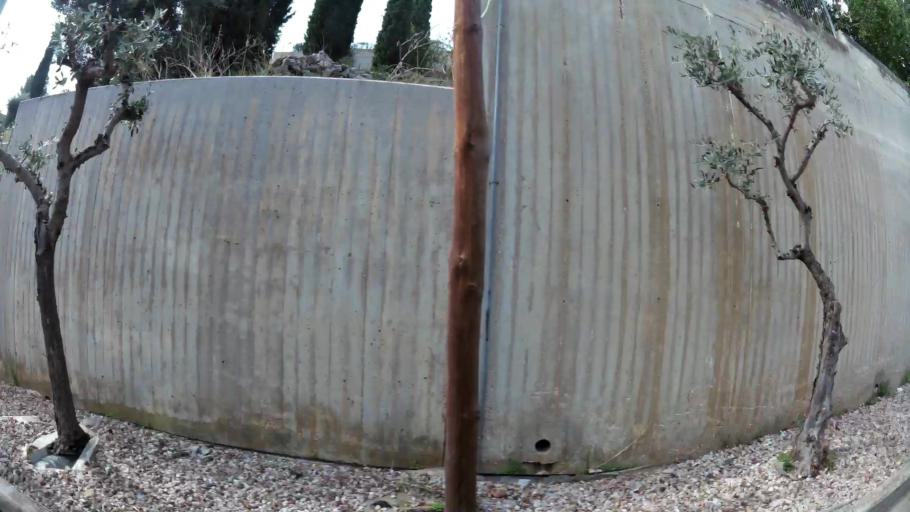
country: GR
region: Attica
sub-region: Nomarchia Athinas
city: Psychiko
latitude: 38.0121
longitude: 23.7650
